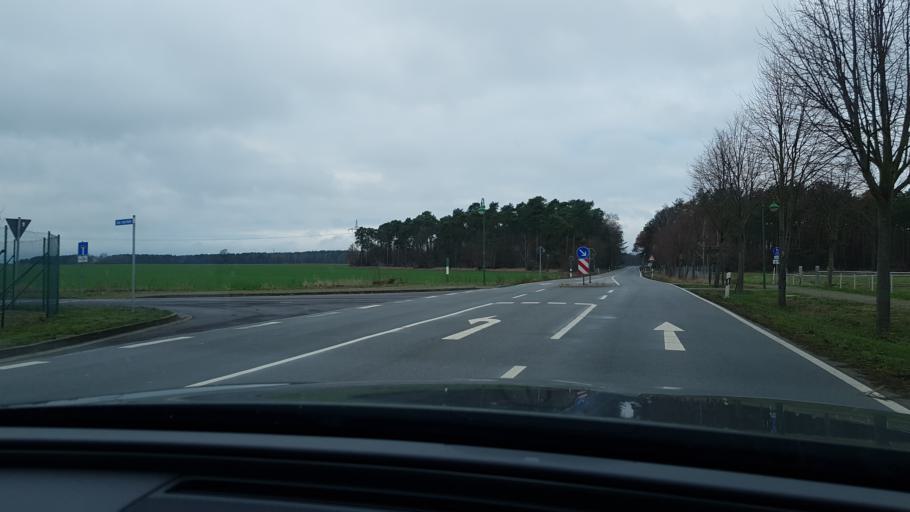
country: DE
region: Lower Saxony
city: Bahrdorf
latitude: 52.4154
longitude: 11.0632
